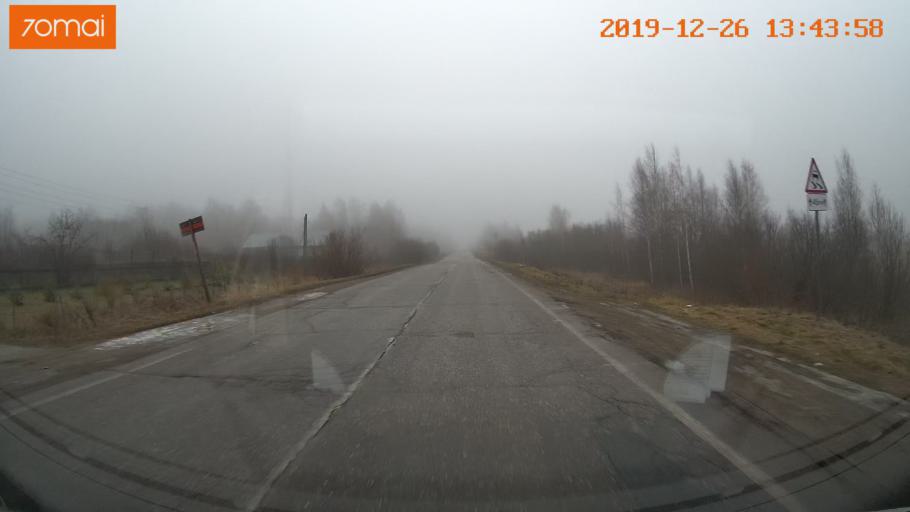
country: RU
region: Vologda
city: Sheksna
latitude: 58.7056
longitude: 38.5001
